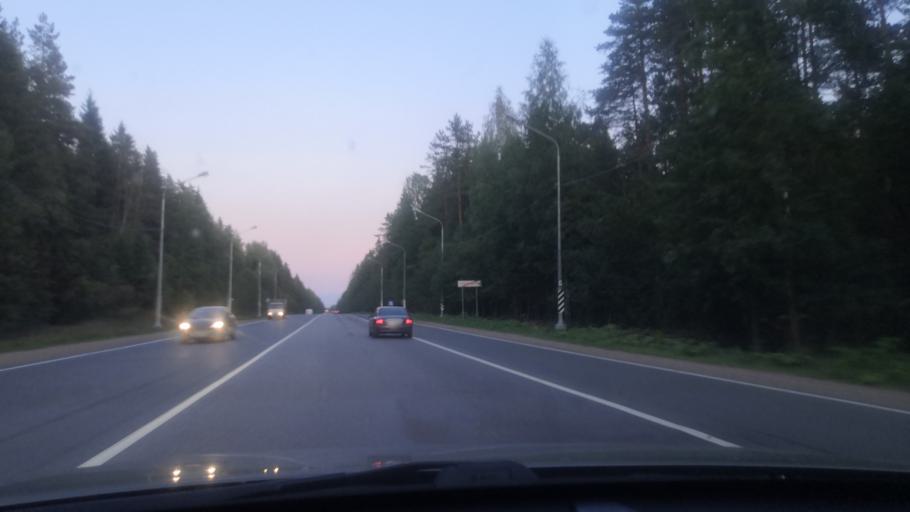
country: RU
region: St.-Petersburg
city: Pesochnyy
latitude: 60.1877
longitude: 30.1049
